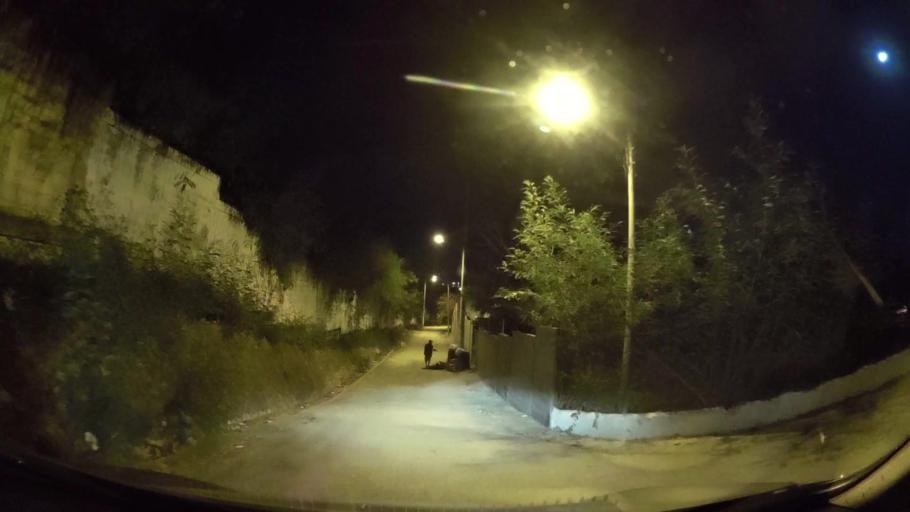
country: CO
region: Bolivar
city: Cartagena
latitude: 10.3860
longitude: -75.4971
